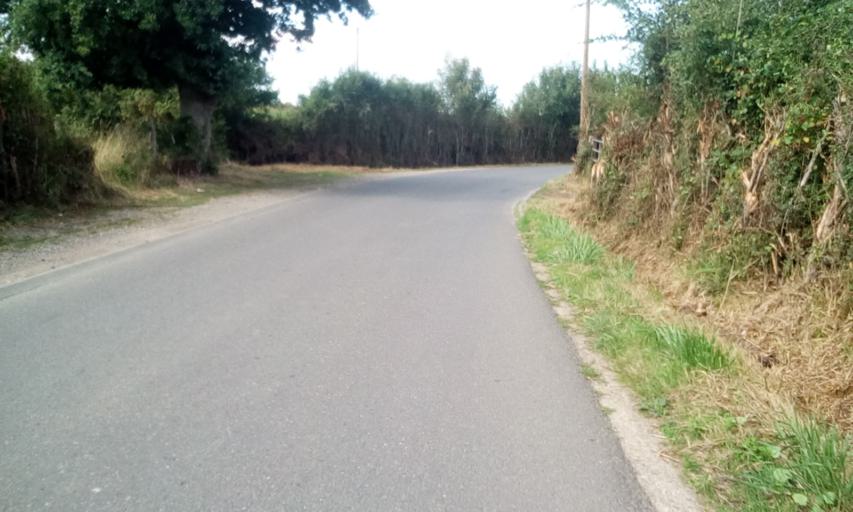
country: FR
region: Lower Normandy
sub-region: Departement du Calvados
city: Argences
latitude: 49.1267
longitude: -0.1320
